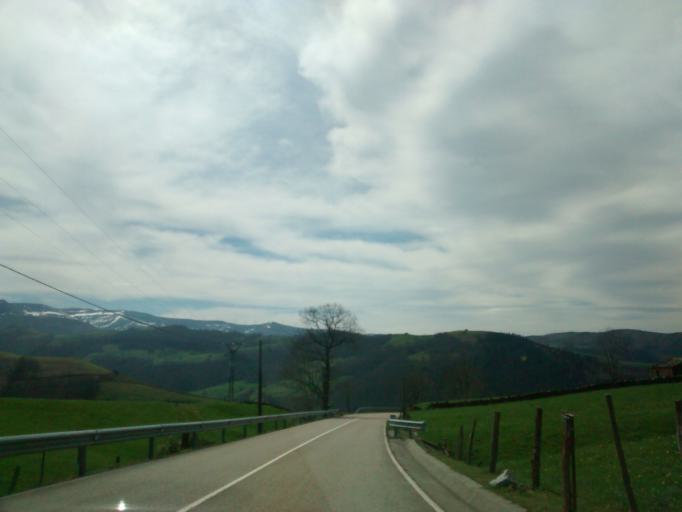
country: ES
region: Cantabria
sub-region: Provincia de Cantabria
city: Vega de Pas
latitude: 43.1671
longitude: -3.7741
